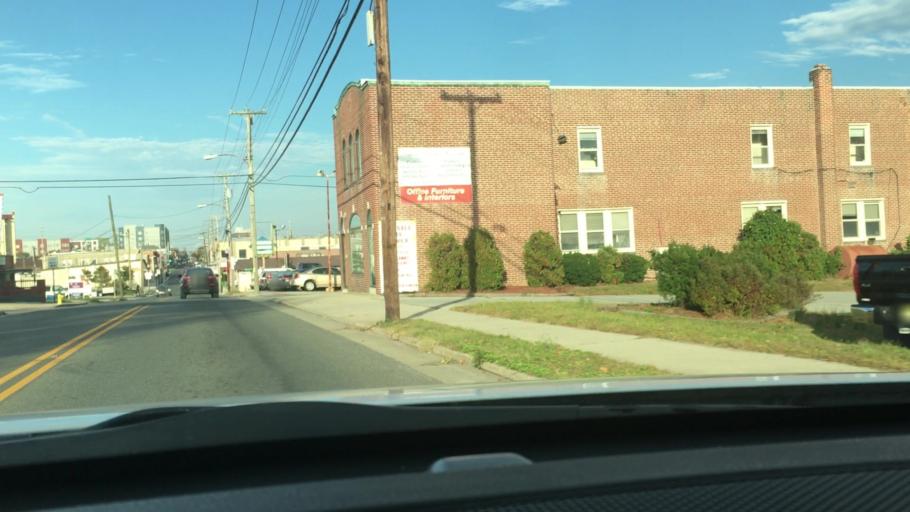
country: US
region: New Jersey
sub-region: Atlantic County
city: Pleasantville
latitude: 39.3874
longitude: -74.5264
